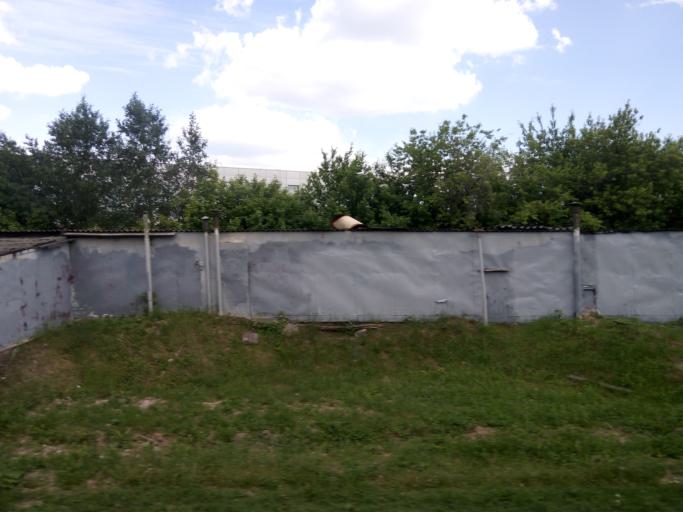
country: RU
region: Moscow
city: Novyye Cheremushki
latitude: 55.6949
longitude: 37.6154
